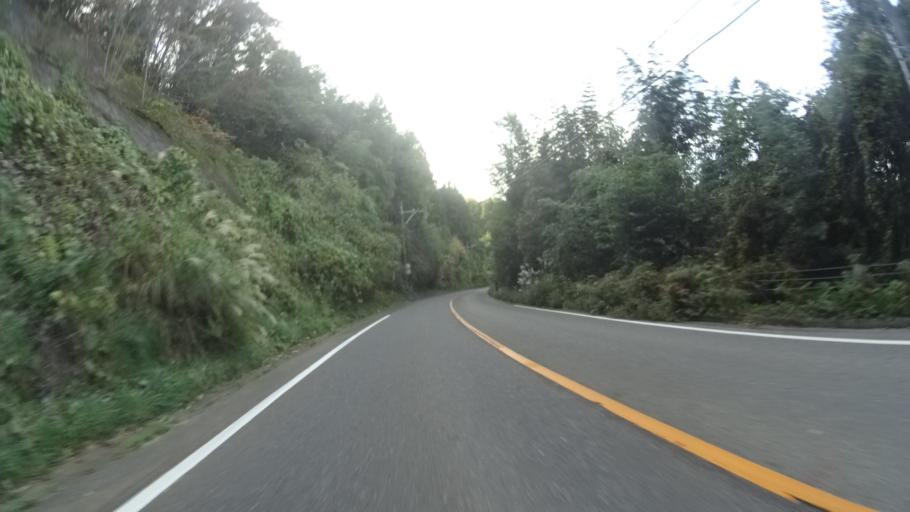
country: JP
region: Ishikawa
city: Nanao
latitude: 37.1771
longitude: 136.7145
